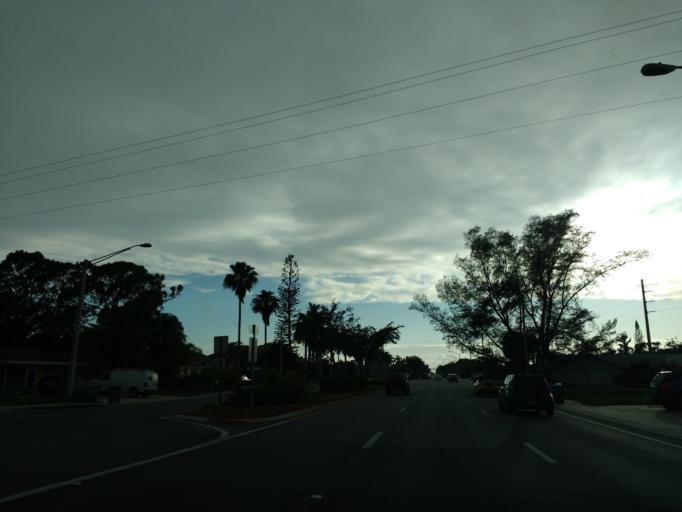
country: US
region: Florida
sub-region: Lee County
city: Cape Coral
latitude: 26.5629
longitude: -81.9775
